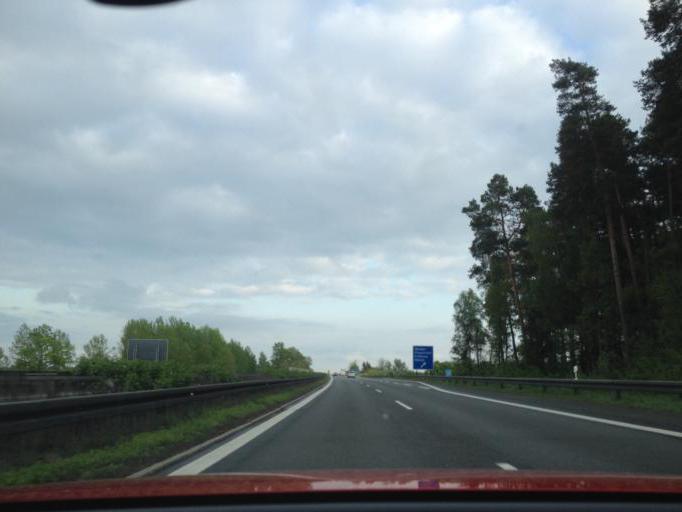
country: DE
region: Bavaria
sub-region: Upper Palatinate
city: Weiden
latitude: 49.6772
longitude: 12.1285
